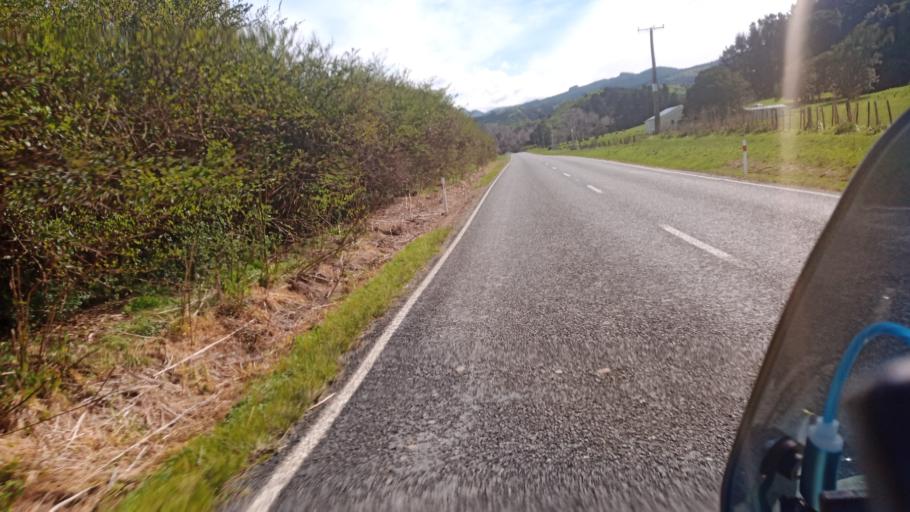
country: NZ
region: Gisborne
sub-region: Gisborne District
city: Gisborne
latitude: -37.8713
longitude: 178.2747
